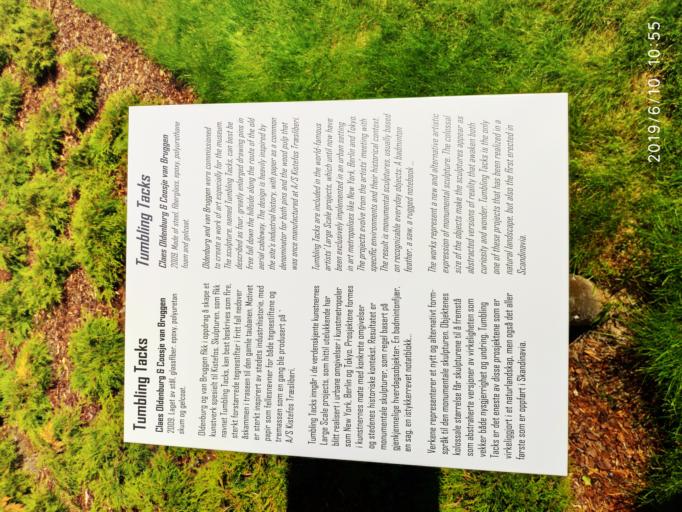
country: NO
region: Oppland
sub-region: Jevnaker
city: Jevnaker
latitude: 60.2231
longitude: 10.3693
